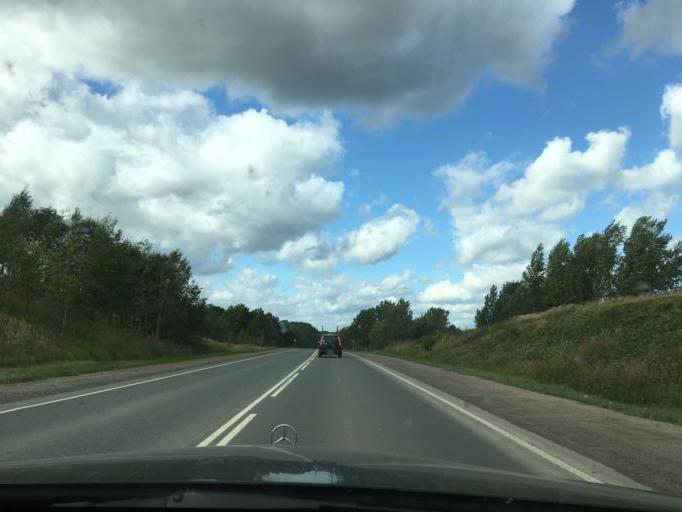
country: RU
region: Pskov
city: Novosokol'niki
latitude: 56.3000
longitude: 30.2181
